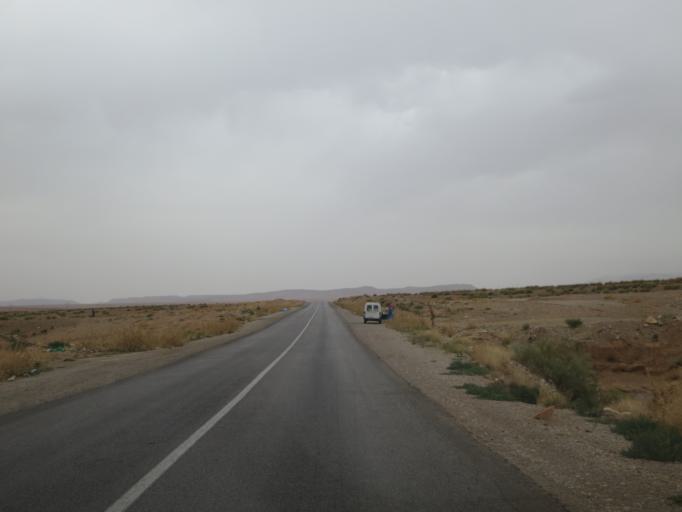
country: MA
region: Meknes-Tafilalet
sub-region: Khenifra
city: Midelt
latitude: 32.6978
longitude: -4.8199
